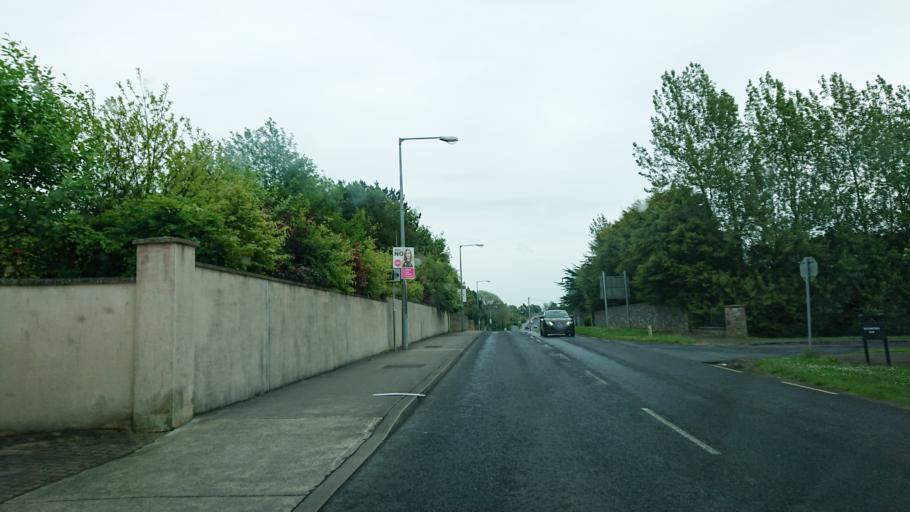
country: IE
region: Munster
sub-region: Waterford
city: Waterford
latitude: 52.2402
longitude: -7.0874
